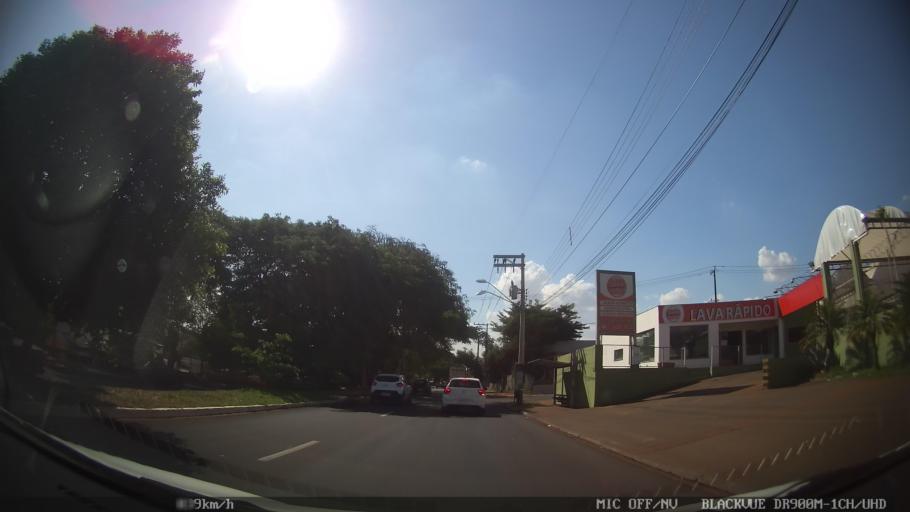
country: BR
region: Sao Paulo
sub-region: Ribeirao Preto
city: Ribeirao Preto
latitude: -21.1939
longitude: -47.8217
